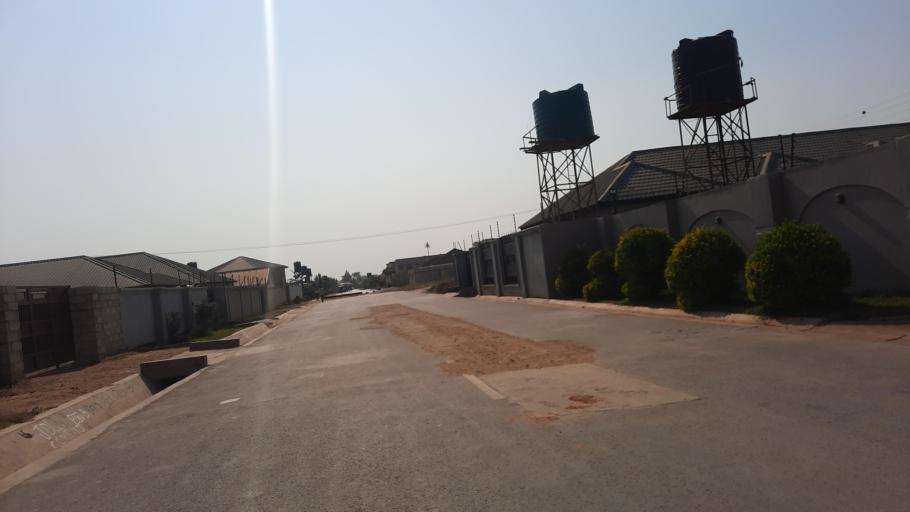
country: ZM
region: Lusaka
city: Lusaka
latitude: -15.3922
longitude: 28.3862
